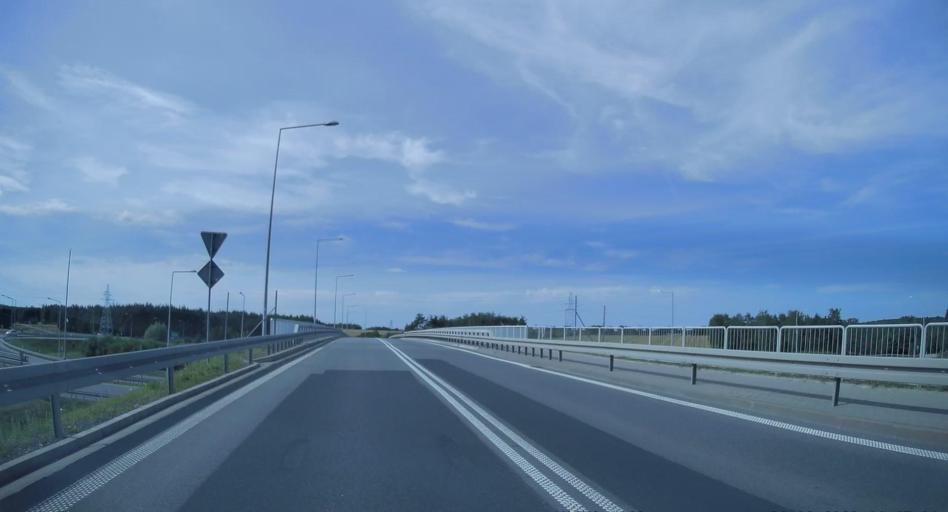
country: PL
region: Lodz Voivodeship
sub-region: Powiat tomaszowski
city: Tomaszow Mazowiecki
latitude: 51.5493
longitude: 19.9894
